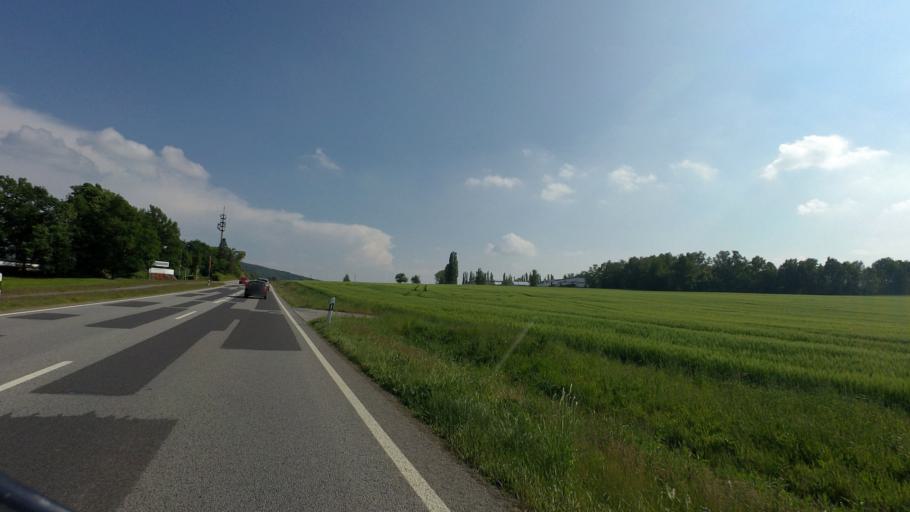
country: DE
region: Saxony
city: Bautzen
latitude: 51.1520
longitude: 14.4352
